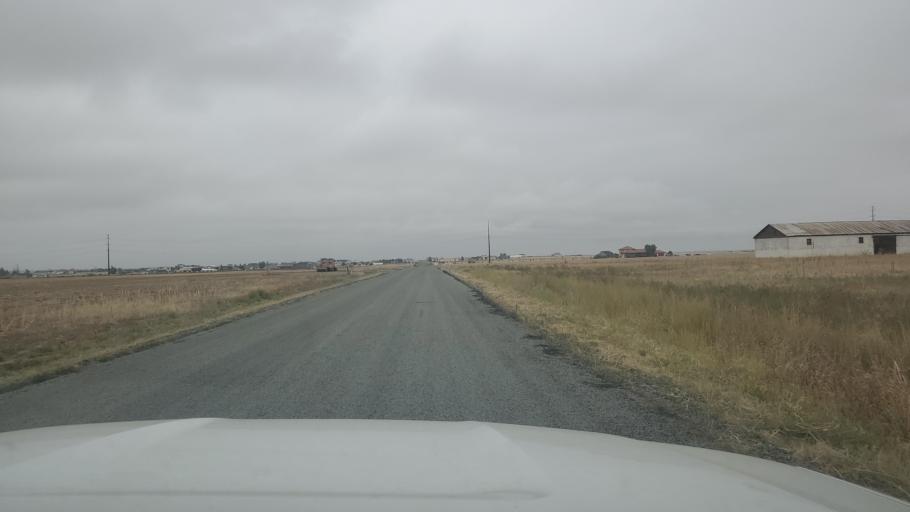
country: US
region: Colorado
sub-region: Weld County
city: Lochbuie
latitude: 39.9379
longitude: -104.6028
